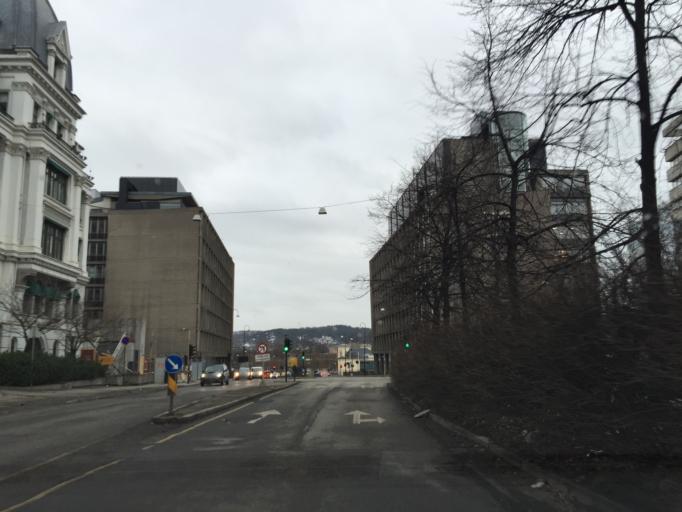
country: NO
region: Oslo
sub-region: Oslo
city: Oslo
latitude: 59.9136
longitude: 10.7261
